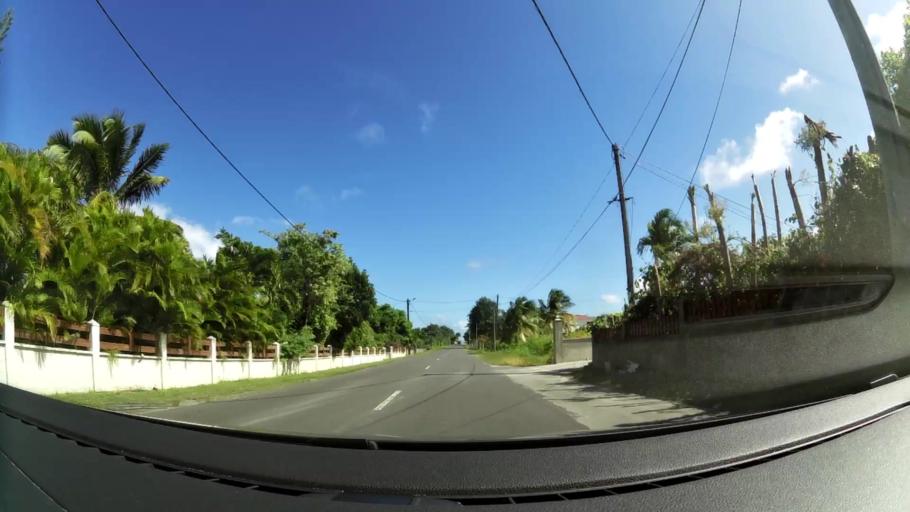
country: GP
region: Guadeloupe
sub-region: Guadeloupe
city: Le Moule
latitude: 16.3071
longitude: -61.3087
